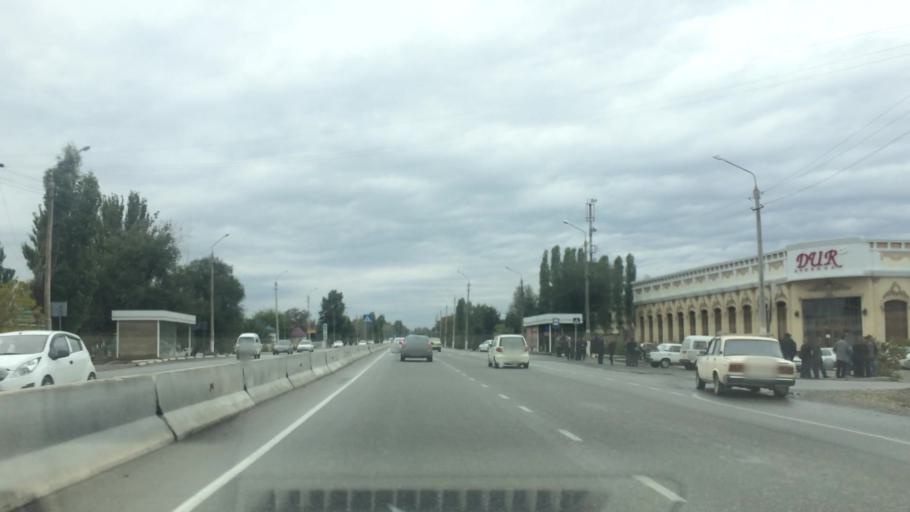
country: UZ
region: Jizzax
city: Jizzax
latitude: 40.0021
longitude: 67.5924
